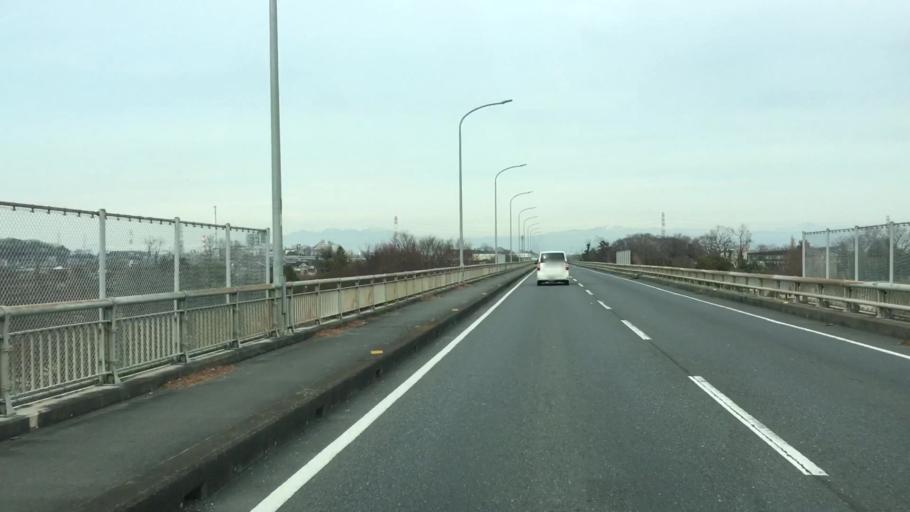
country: JP
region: Saitama
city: Kumagaya
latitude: 36.1402
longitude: 139.3232
